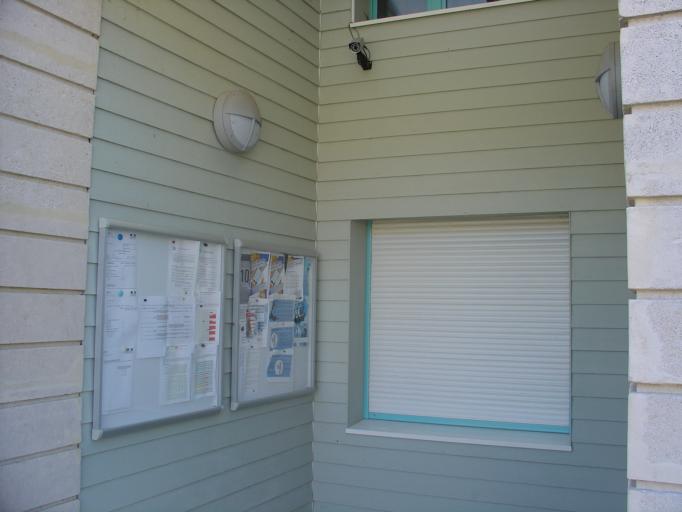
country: FR
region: Lorraine
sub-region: Departement de Meurthe-et-Moselle
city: Ecrouves
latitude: 48.7664
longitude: 5.8612
